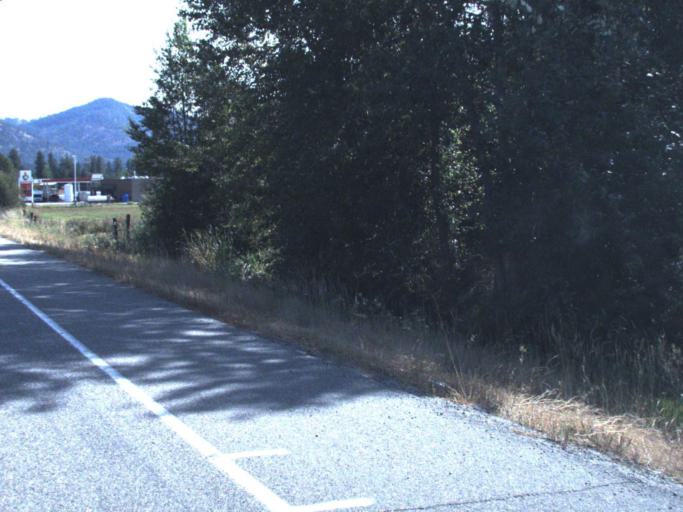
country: US
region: Washington
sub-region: Stevens County
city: Chewelah
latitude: 48.2880
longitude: -117.7255
